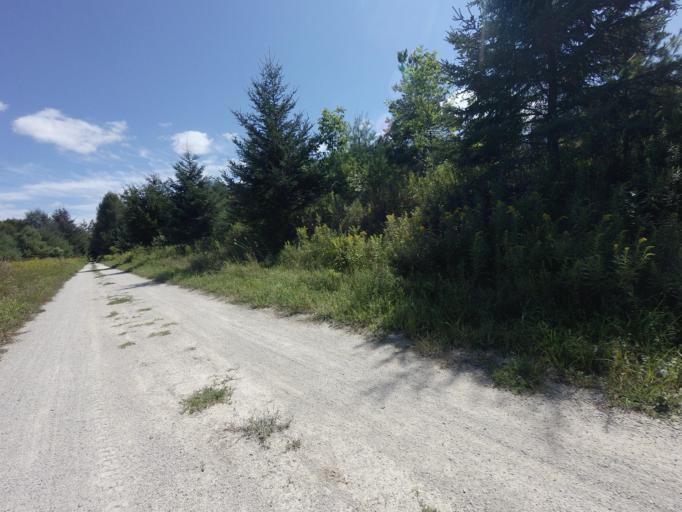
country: CA
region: Ontario
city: Orangeville
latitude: 43.7768
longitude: -80.1125
